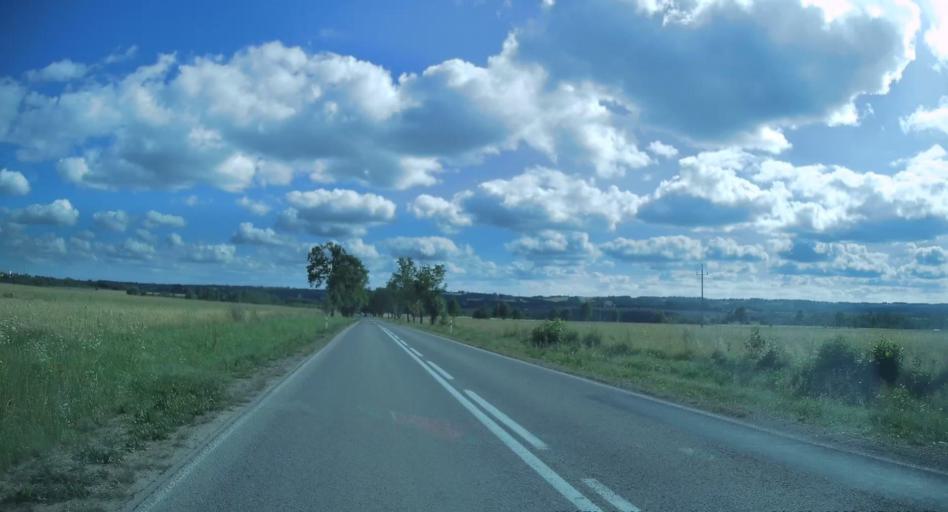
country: PL
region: Swietokrzyskie
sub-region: Powiat kielecki
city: Lagow
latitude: 50.7903
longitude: 21.0817
